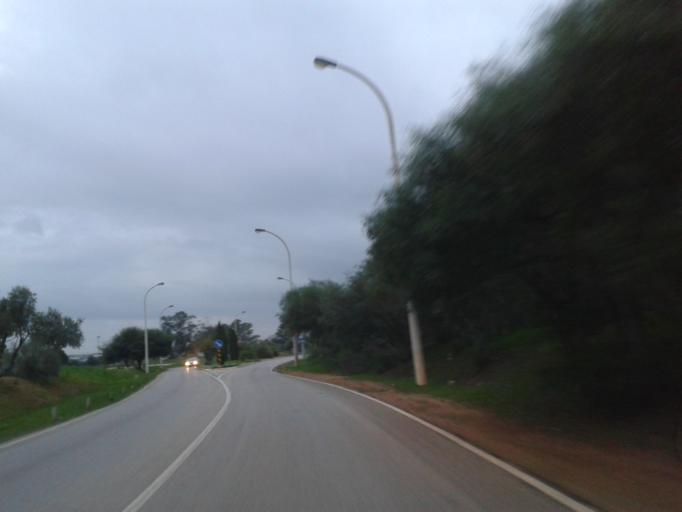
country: PT
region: Faro
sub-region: Loule
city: Boliqueime
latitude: 37.1117
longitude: -8.1445
